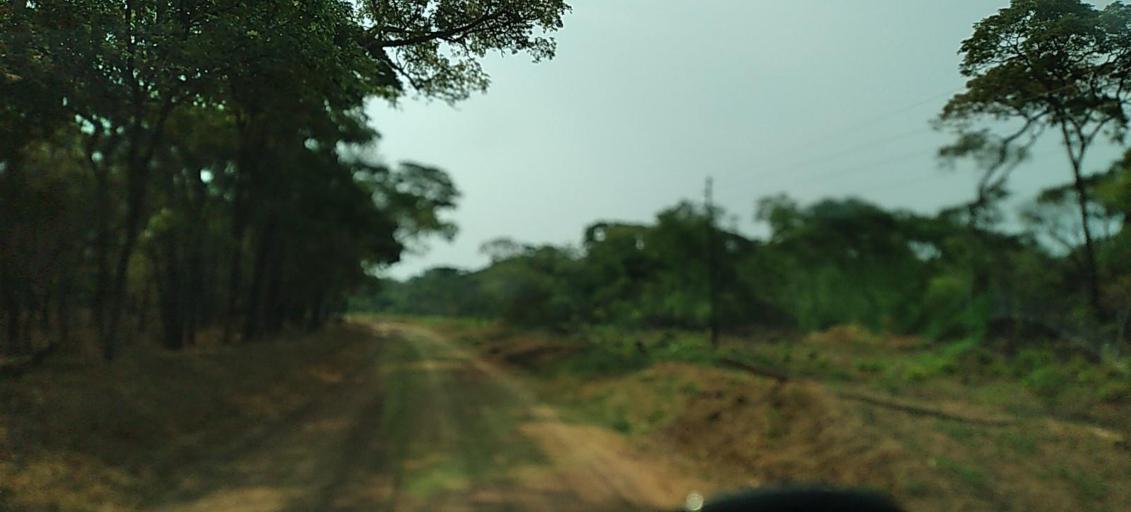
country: ZM
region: North-Western
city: Solwezi
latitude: -12.6867
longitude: 26.3960
